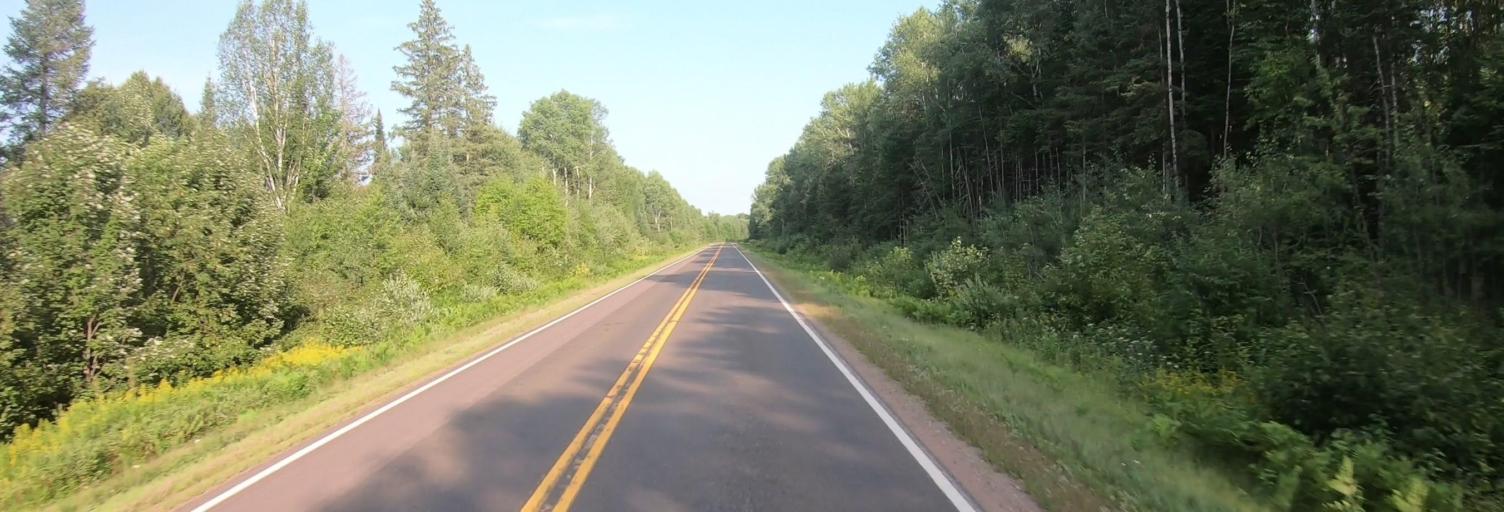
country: US
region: Wisconsin
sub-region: Ashland County
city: Ashland
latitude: 46.2565
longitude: -90.8383
